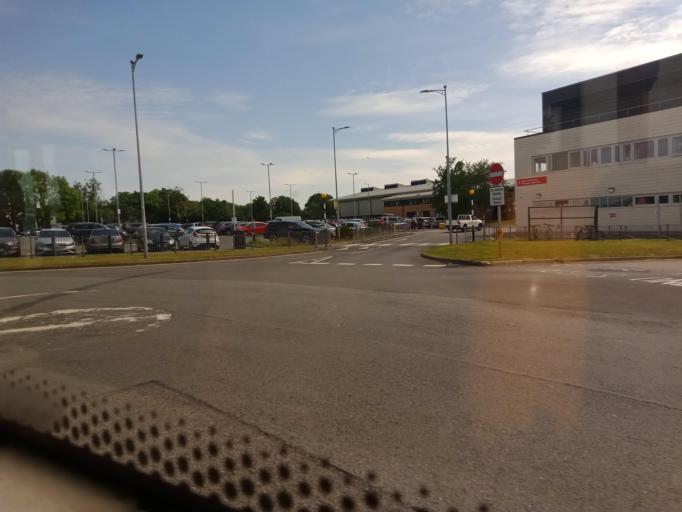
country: GB
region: Wales
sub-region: Anglesey
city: Menai Bridge
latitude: 53.2100
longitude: -4.1606
